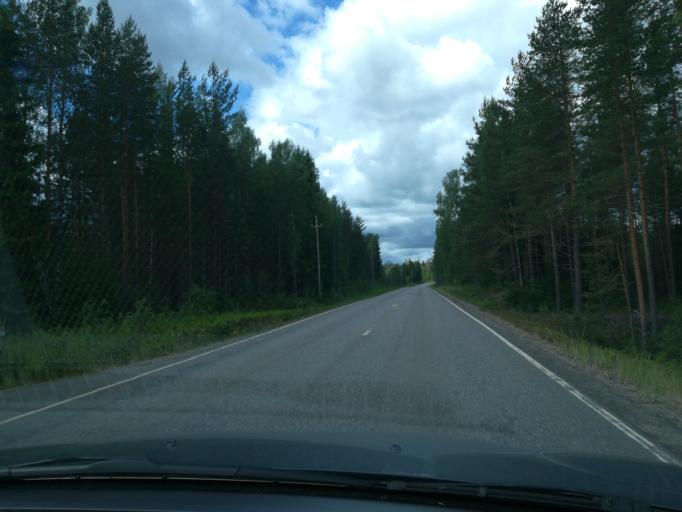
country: FI
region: Southern Savonia
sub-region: Mikkeli
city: Maentyharju
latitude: 61.3622
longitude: 27.0429
